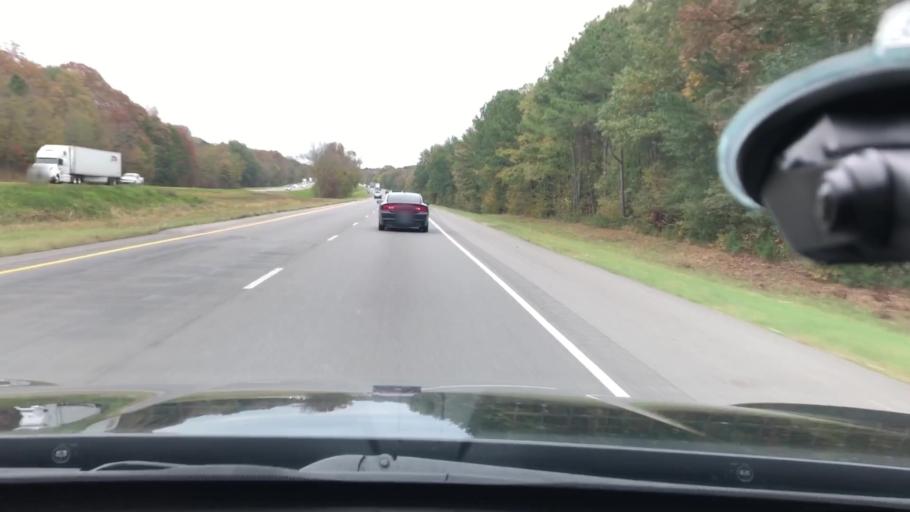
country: US
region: Arkansas
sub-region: Hempstead County
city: Hope
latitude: 33.6307
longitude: -93.7241
